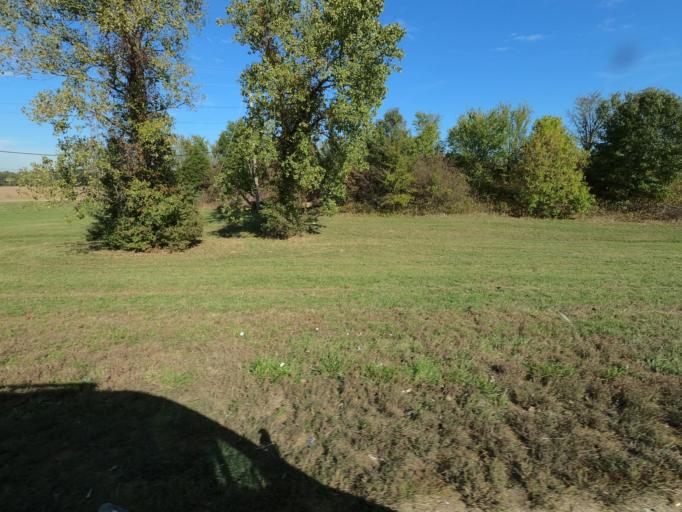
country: US
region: Tennessee
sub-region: Shelby County
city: Millington
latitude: 35.3303
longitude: -89.9206
